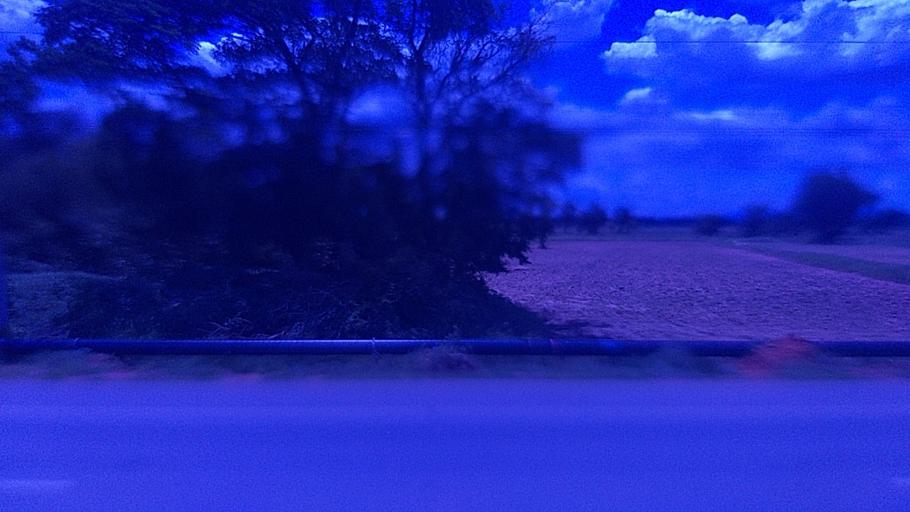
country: TH
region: Chaiyaphum
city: Noen Sa-nga
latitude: 15.6773
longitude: 101.9936
